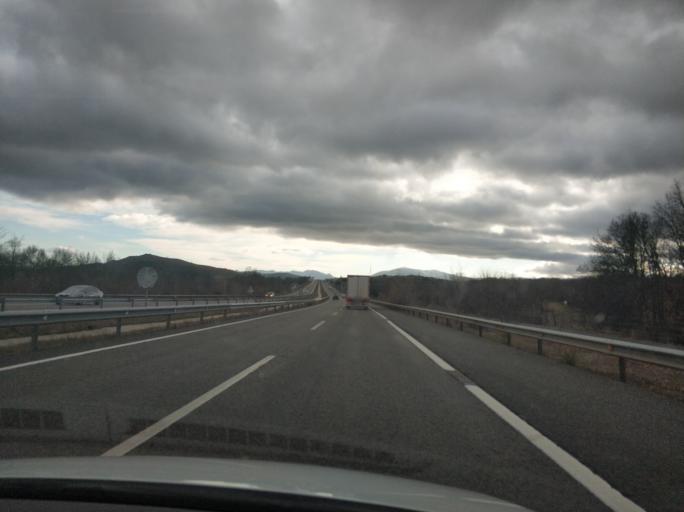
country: ES
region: Madrid
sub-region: Provincia de Madrid
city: Braojos
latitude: 41.0518
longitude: -3.6151
